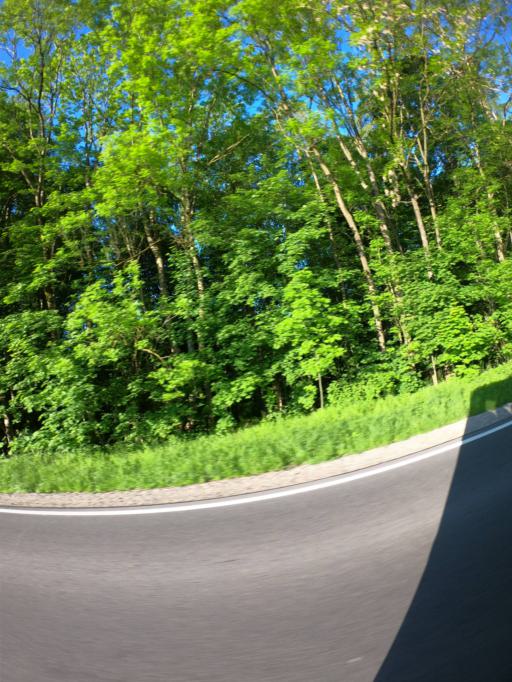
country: DE
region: Bavaria
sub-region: Upper Bavaria
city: Inning am Holz
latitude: 48.3368
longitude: 12.0374
